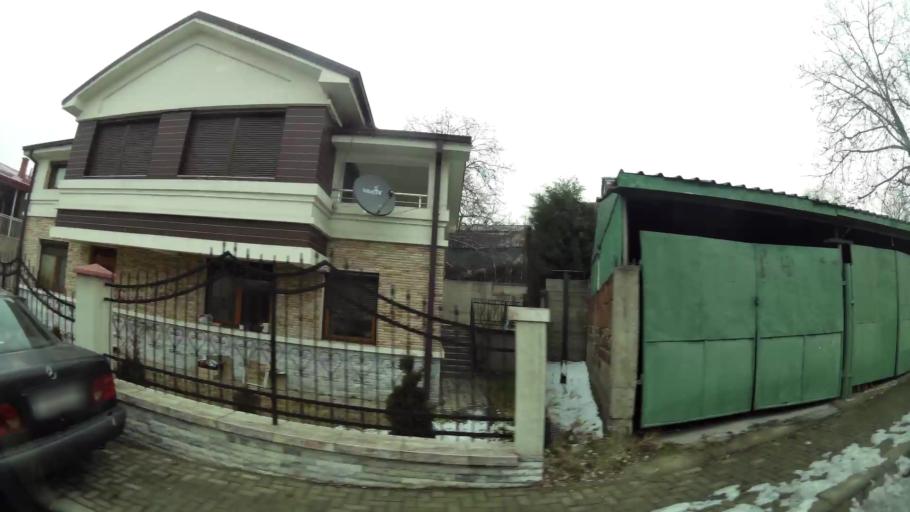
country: MK
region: Cair
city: Cair
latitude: 42.0135
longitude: 21.4565
